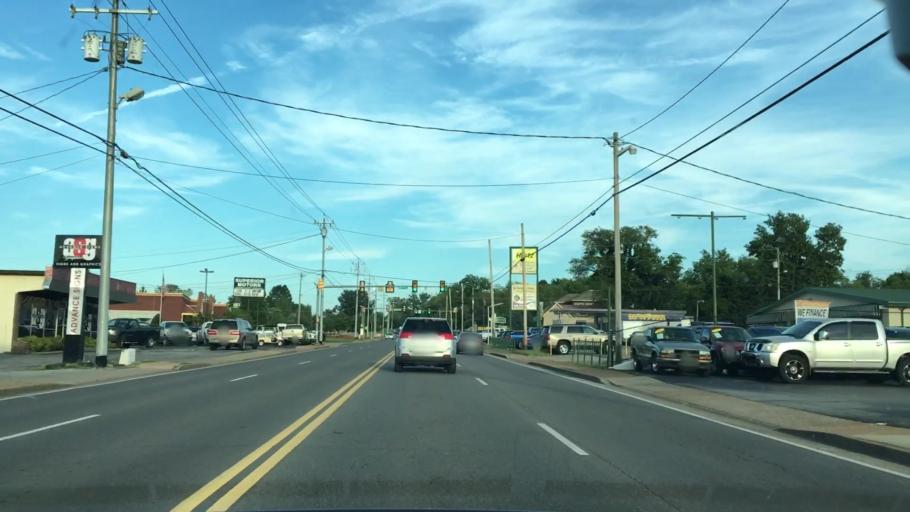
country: US
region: Tennessee
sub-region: Wilson County
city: Lebanon
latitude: 36.2110
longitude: -86.3137
